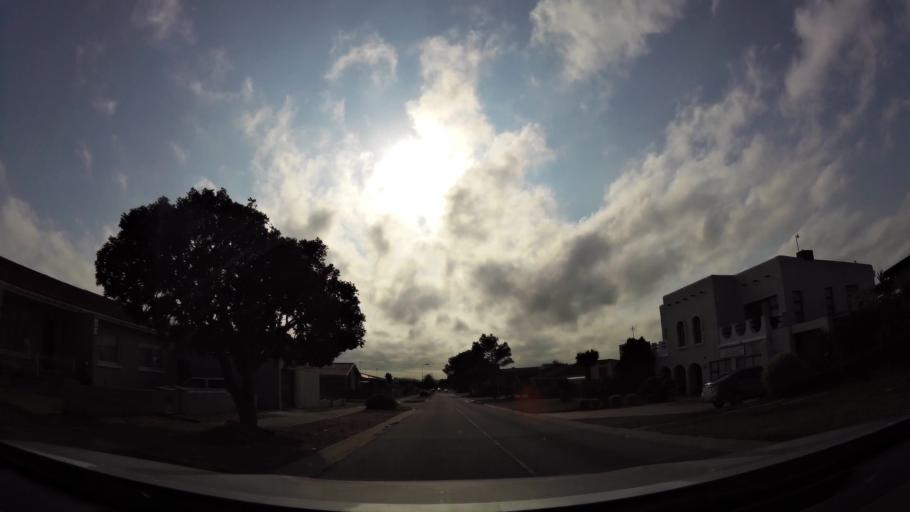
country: ZA
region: Eastern Cape
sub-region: Nelson Mandela Bay Metropolitan Municipality
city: Port Elizabeth
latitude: -33.9221
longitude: 25.5604
